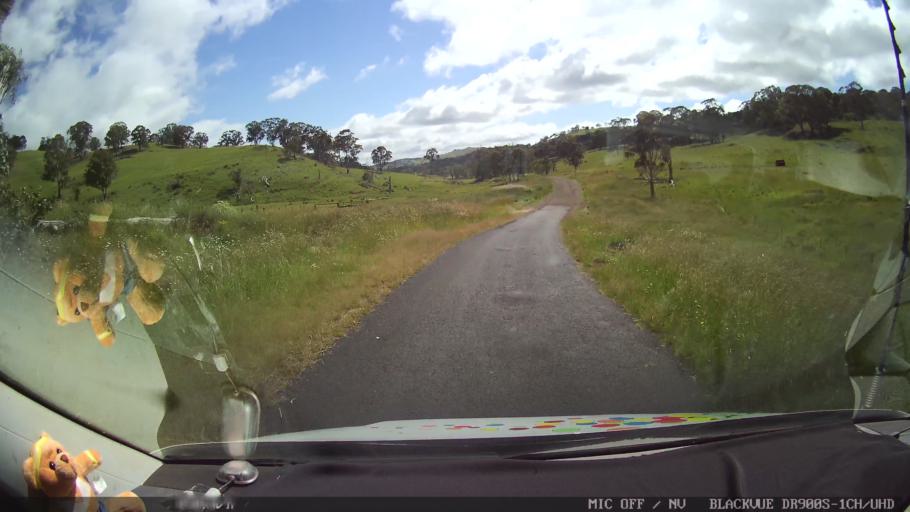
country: AU
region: New South Wales
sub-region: Guyra
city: Guyra
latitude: -29.9992
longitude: 151.6745
